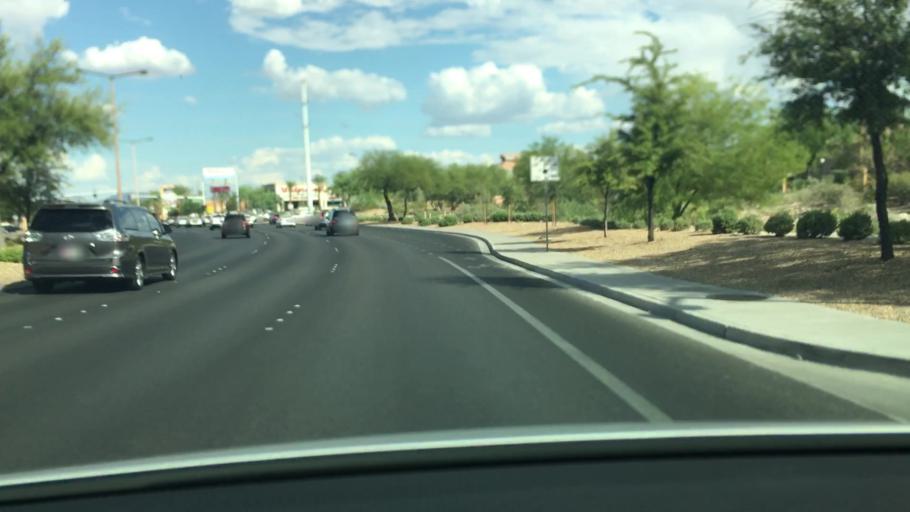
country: US
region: Nevada
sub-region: Clark County
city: Spring Valley
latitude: 36.1963
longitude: -115.2625
